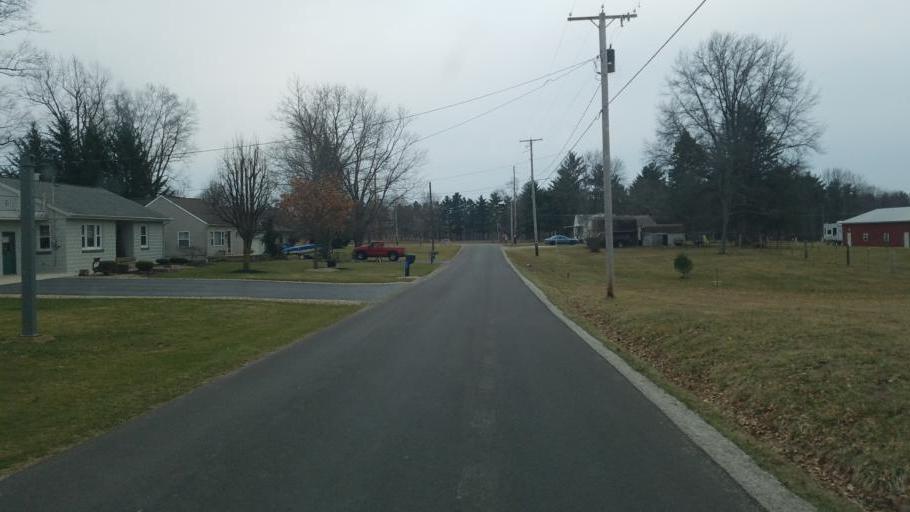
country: US
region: Ohio
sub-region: Crawford County
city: Galion
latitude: 40.7140
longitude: -82.8205
